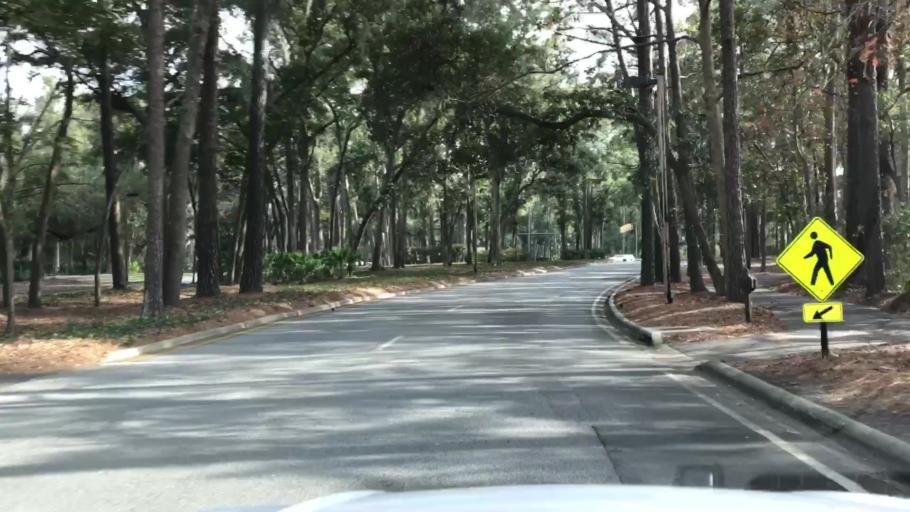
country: US
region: South Carolina
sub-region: Beaufort County
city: Hilton Head Island
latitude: 32.2161
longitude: -80.7217
